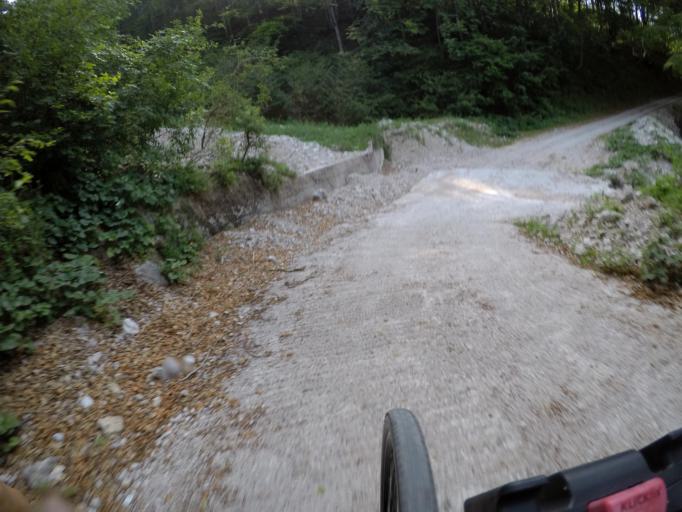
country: IT
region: Friuli Venezia Giulia
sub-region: Provincia di Udine
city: Resiutta
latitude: 46.3350
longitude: 13.2078
